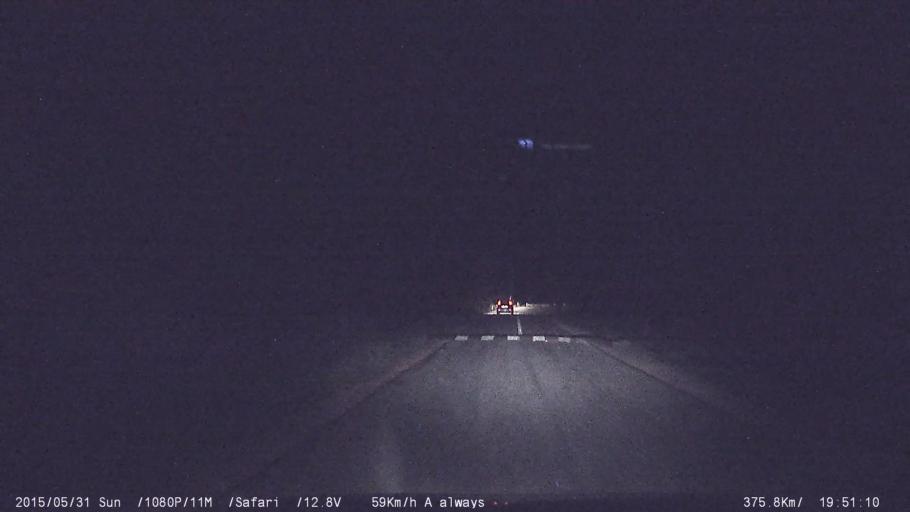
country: IN
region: Karnataka
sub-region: Mandya
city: Malavalli
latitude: 12.3288
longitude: 77.0752
